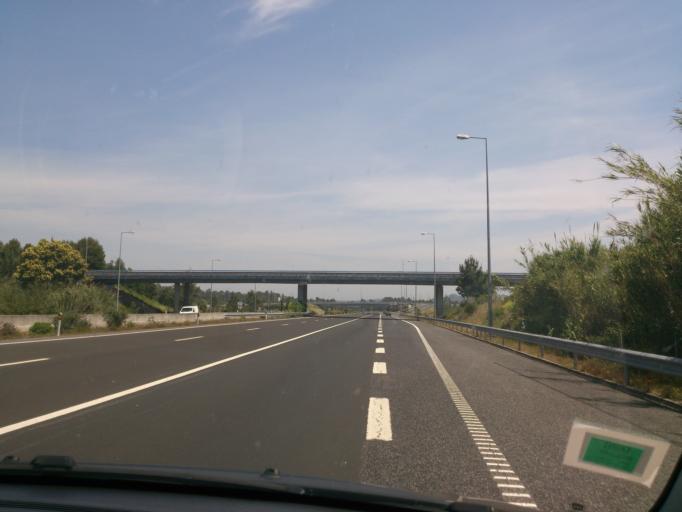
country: PT
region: Leiria
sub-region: Alcobaca
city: Alcobaca
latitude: 39.5849
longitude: -9.0141
